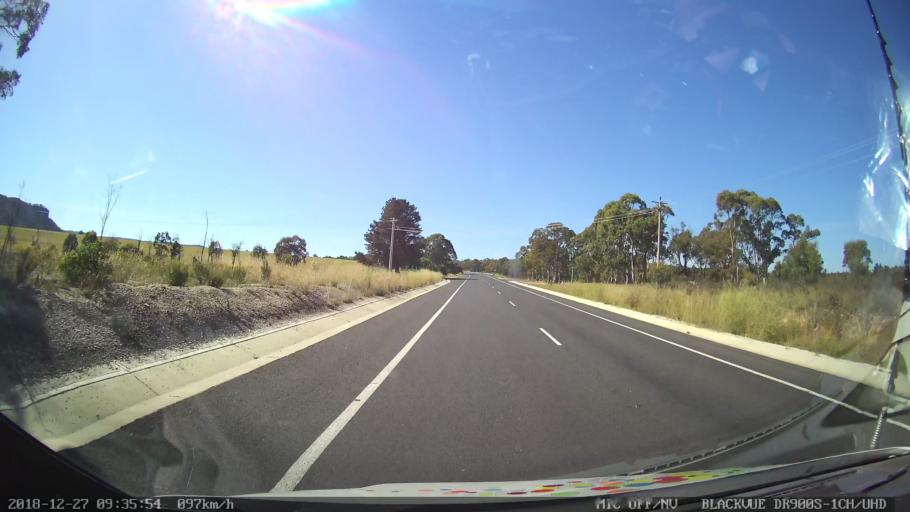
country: AU
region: New South Wales
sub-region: Lithgow
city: Portland
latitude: -33.2448
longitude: 150.0326
